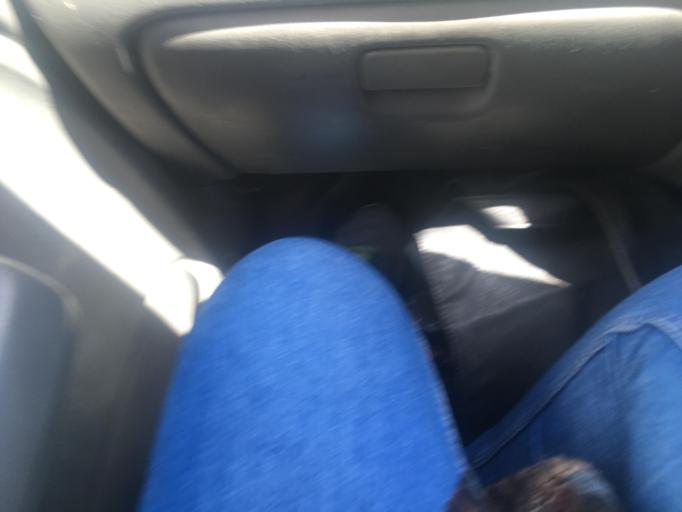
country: PK
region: Gilgit-Baltistan
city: Skardu
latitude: 35.2961
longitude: 75.6339
